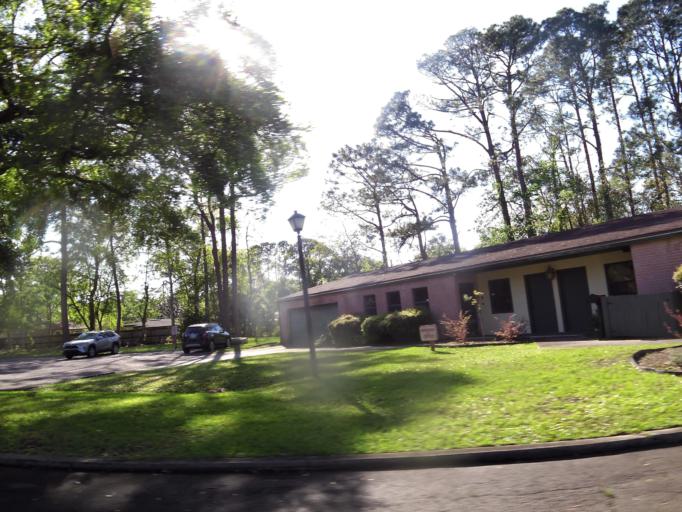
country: US
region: Florida
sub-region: Duval County
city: Jacksonville
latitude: 30.2801
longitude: -81.5980
